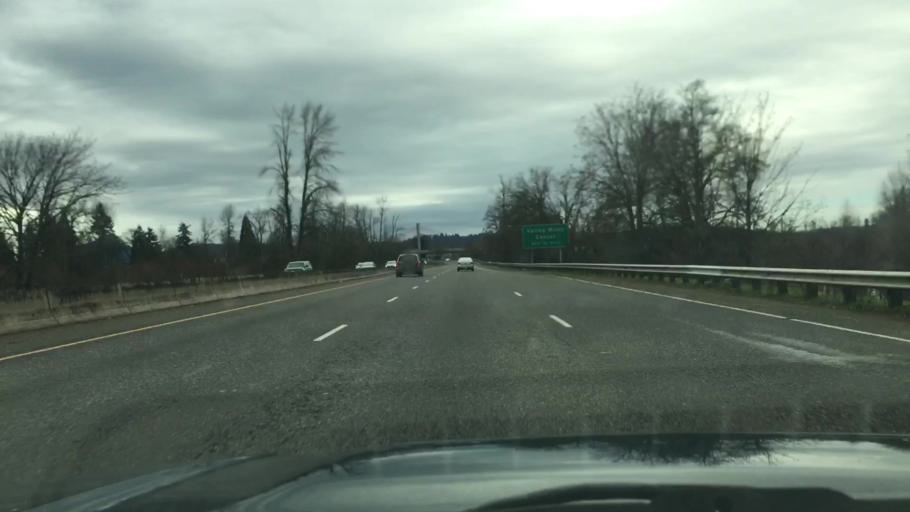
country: US
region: Oregon
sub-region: Lane County
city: Eugene
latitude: 44.0809
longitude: -123.1040
